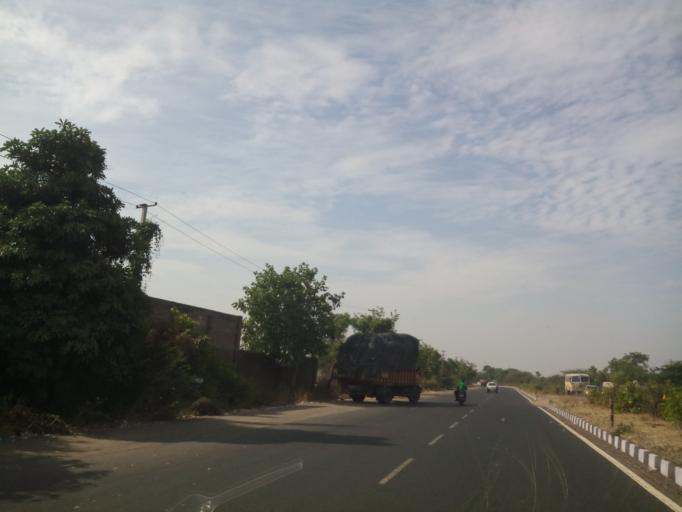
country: IN
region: Gujarat
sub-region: Rajkot
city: Rajkot
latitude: 22.3408
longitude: 70.9053
